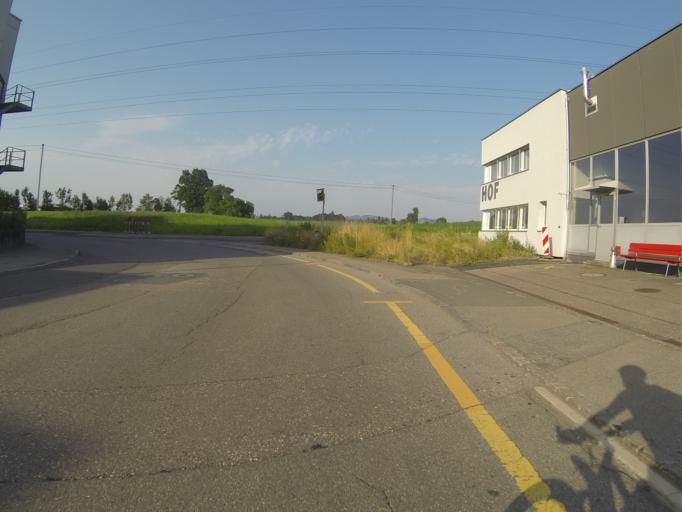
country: CH
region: Lucerne
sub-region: Hochdorf District
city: Emmen
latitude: 47.0655
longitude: 8.2916
